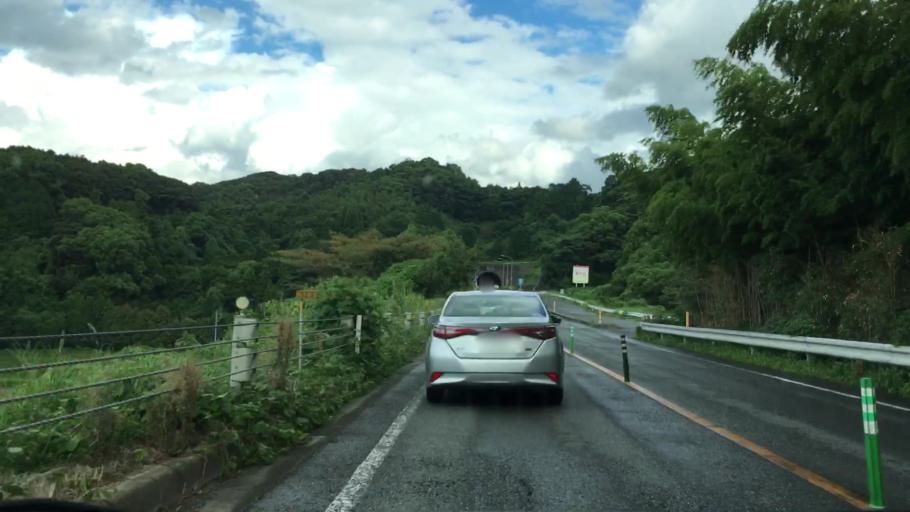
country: JP
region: Fukuoka
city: Maebaru-chuo
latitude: 33.5041
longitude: 130.1033
